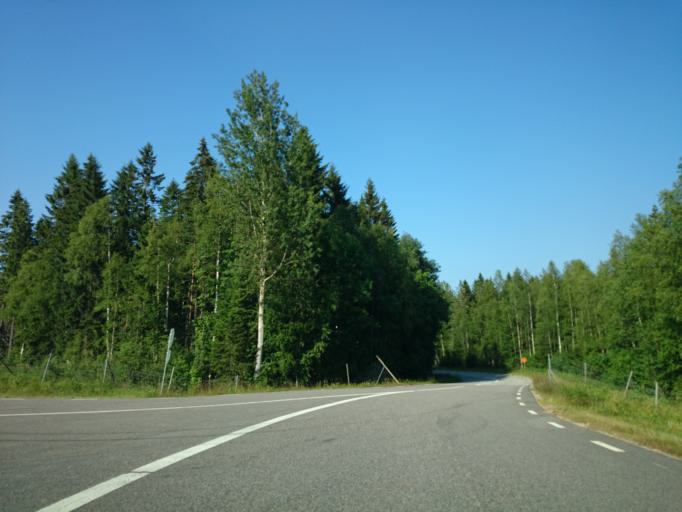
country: SE
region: Vaesternorrland
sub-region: Sundsvalls Kommun
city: Njurundabommen
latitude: 62.2101
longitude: 17.3740
